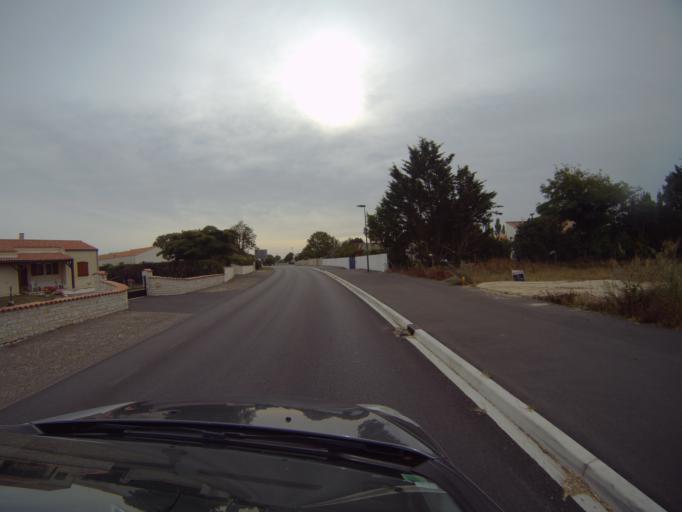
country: FR
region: Pays de la Loire
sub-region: Departement de la Vendee
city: Angles
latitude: 46.4060
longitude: -1.3902
